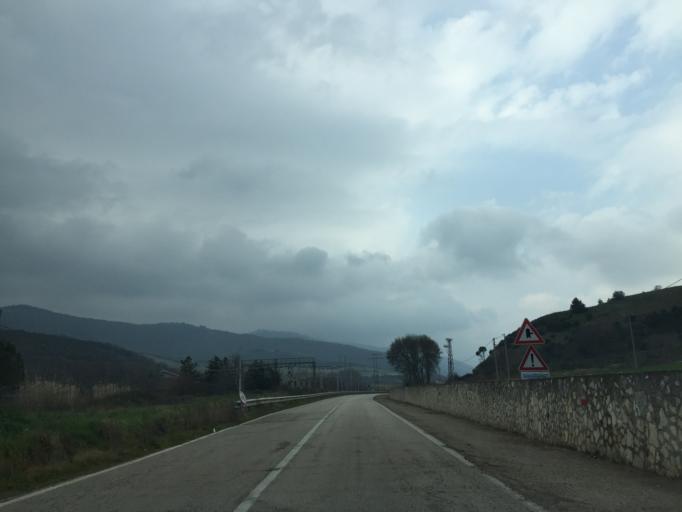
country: IT
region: Apulia
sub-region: Provincia di Foggia
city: Bovino
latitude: 41.2778
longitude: 15.3673
